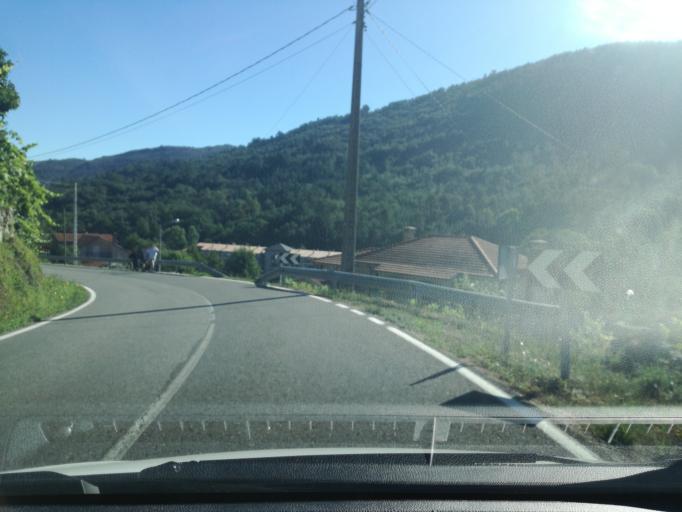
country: ES
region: Galicia
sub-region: Provincia de Ourense
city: Lobios
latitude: 41.8600
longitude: -8.1095
